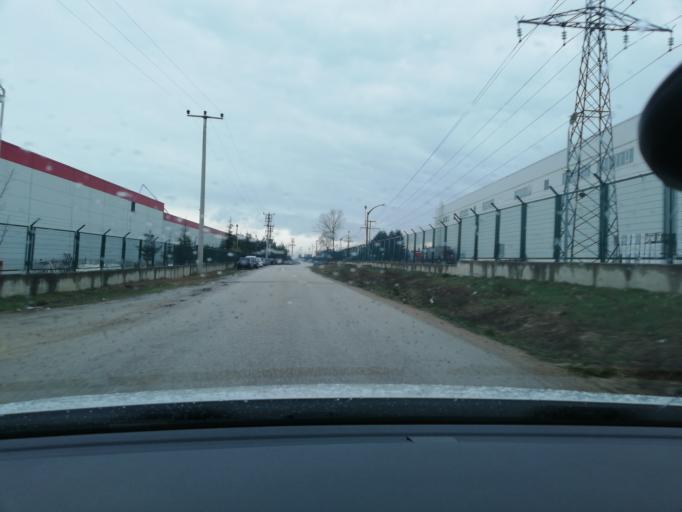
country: TR
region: Bolu
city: Bolu
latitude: 40.7611
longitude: 31.6467
